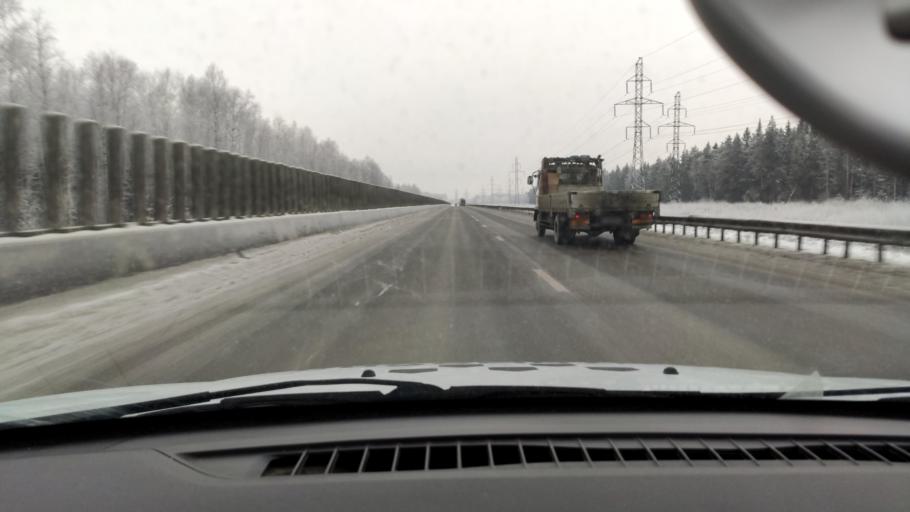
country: RU
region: Perm
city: Overyata
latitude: 58.0366
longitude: 55.9424
